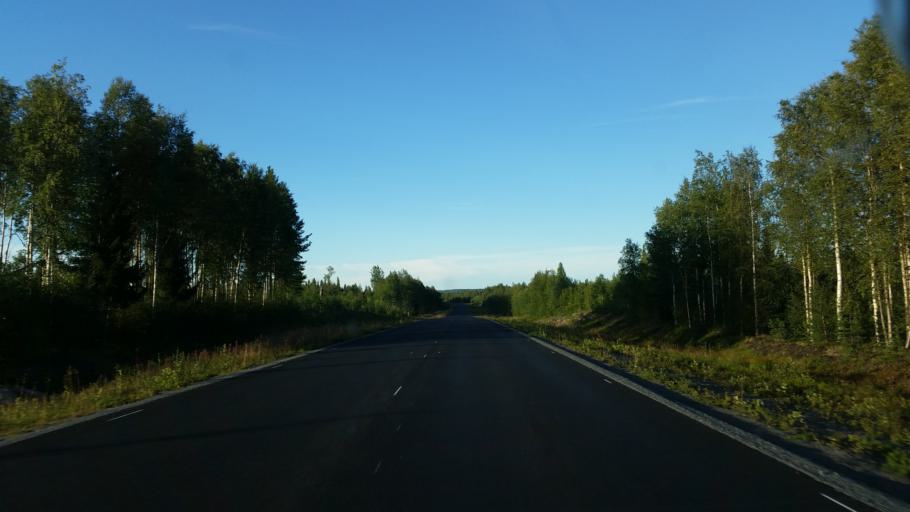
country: SE
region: Vaesterbotten
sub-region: Dorotea Kommun
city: Dorotea
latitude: 64.3231
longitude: 16.6190
